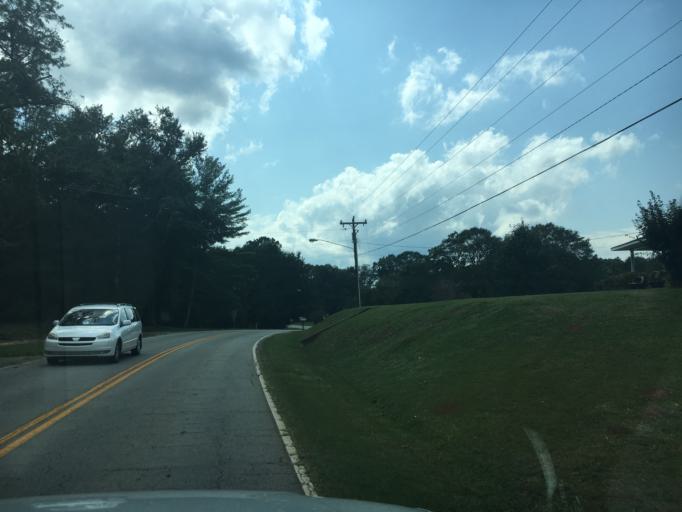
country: US
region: South Carolina
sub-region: Pickens County
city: Central
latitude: 34.8097
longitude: -82.8180
